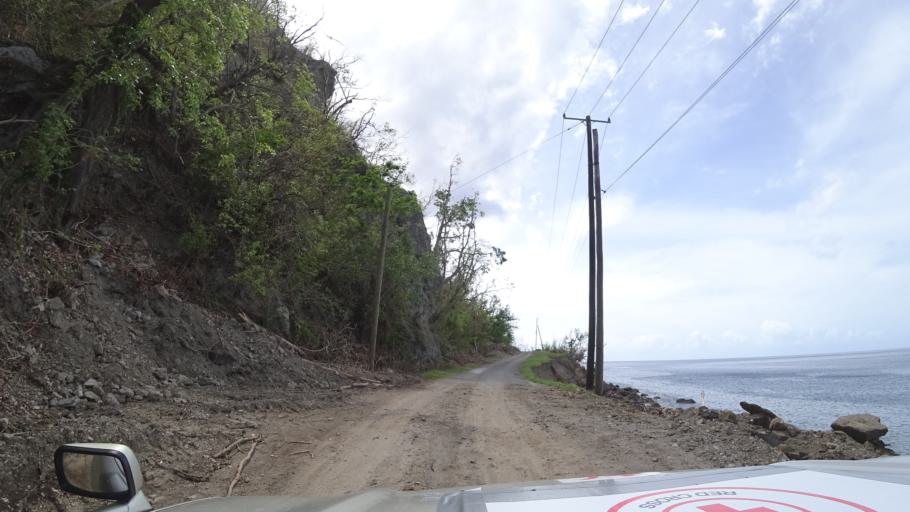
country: DM
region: Saint Luke
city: Pointe Michel
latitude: 15.2534
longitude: -61.3754
